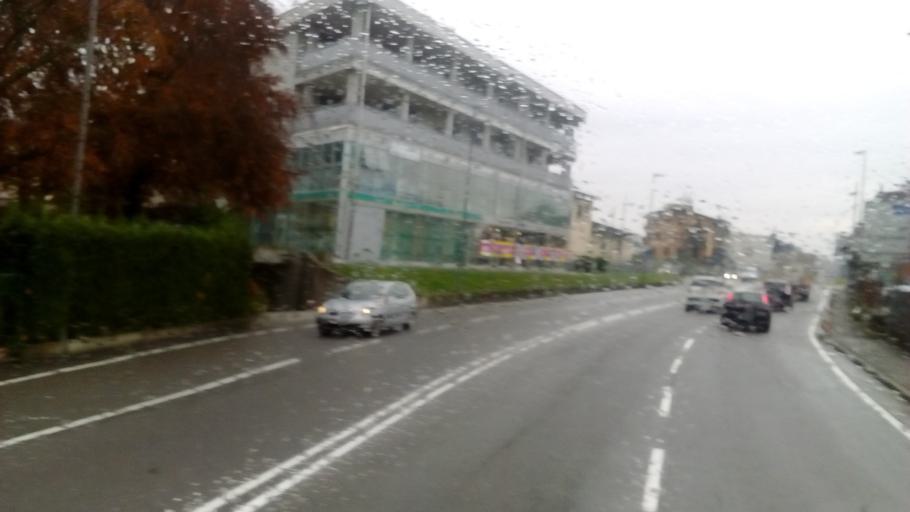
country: IT
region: Lombardy
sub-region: Provincia di Bergamo
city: Villa d'Alme
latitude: 45.7467
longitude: 9.6141
